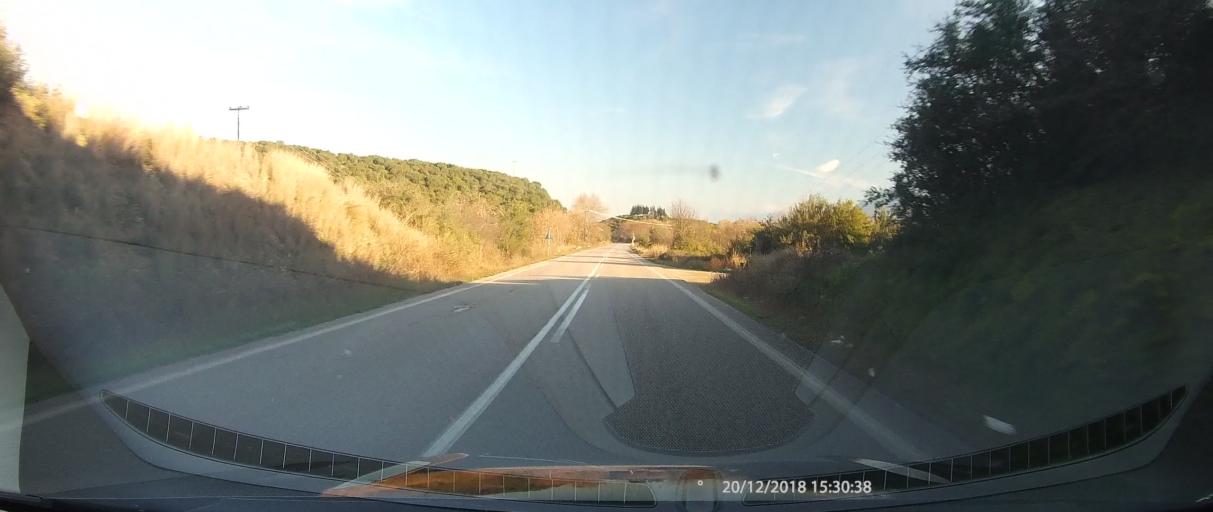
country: GR
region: Central Greece
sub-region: Nomos Fthiotidos
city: Lianokladhion
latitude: 38.9351
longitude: 22.2264
